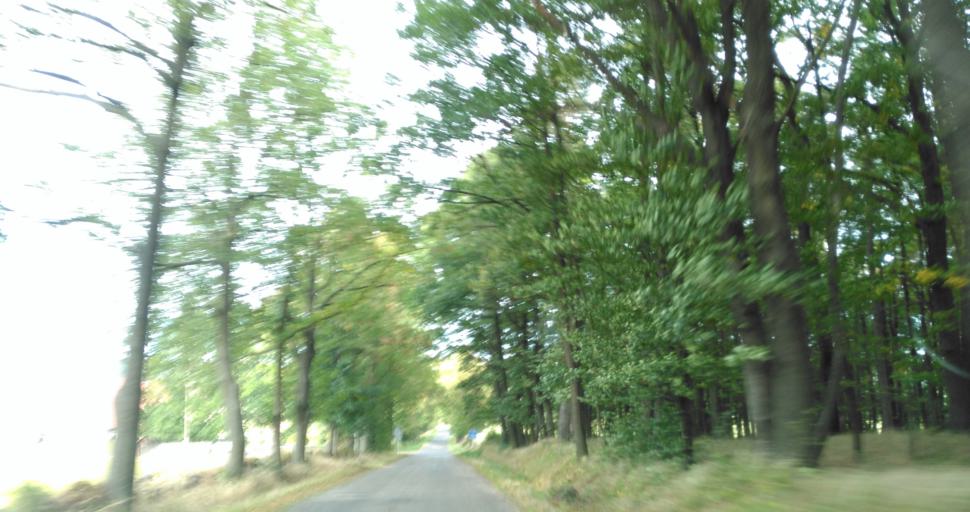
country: CZ
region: Plzensky
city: Zbiroh
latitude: 49.9197
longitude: 13.8195
